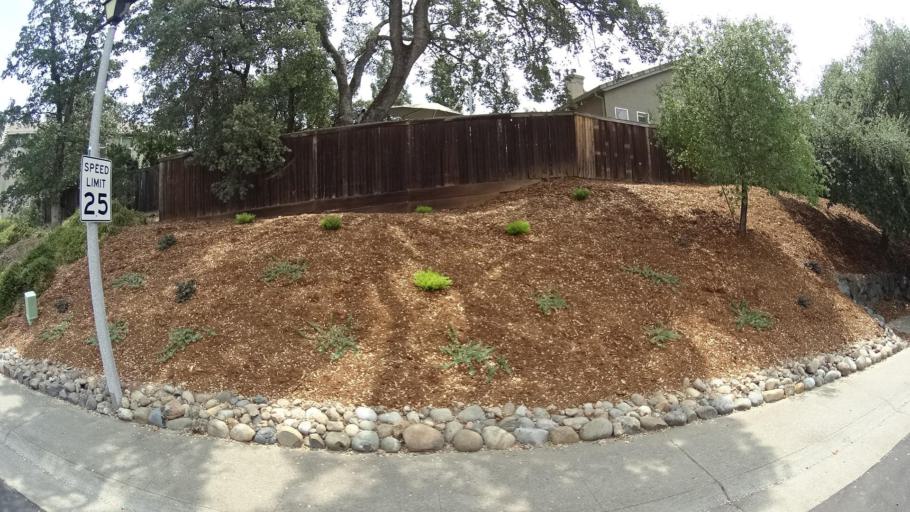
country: US
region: California
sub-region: Placer County
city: Rocklin
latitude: 38.7754
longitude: -121.2158
